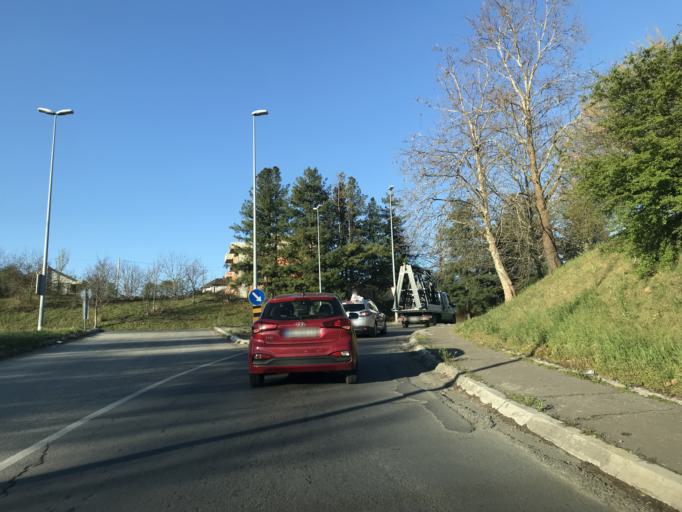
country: RS
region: Autonomna Pokrajina Vojvodina
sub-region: Juznobacki Okrug
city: Petrovaradin
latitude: 45.2275
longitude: 19.8600
